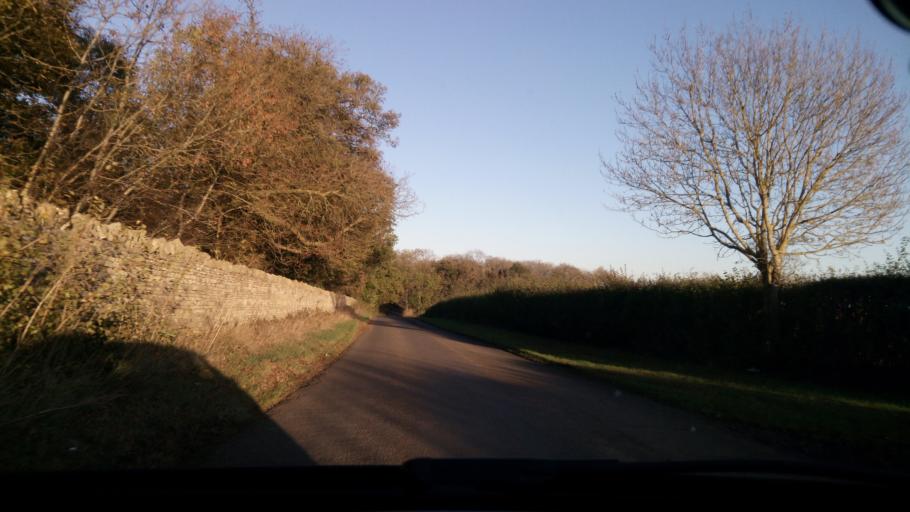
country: GB
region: England
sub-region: Peterborough
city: Wittering
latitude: 52.6238
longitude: -0.4544
